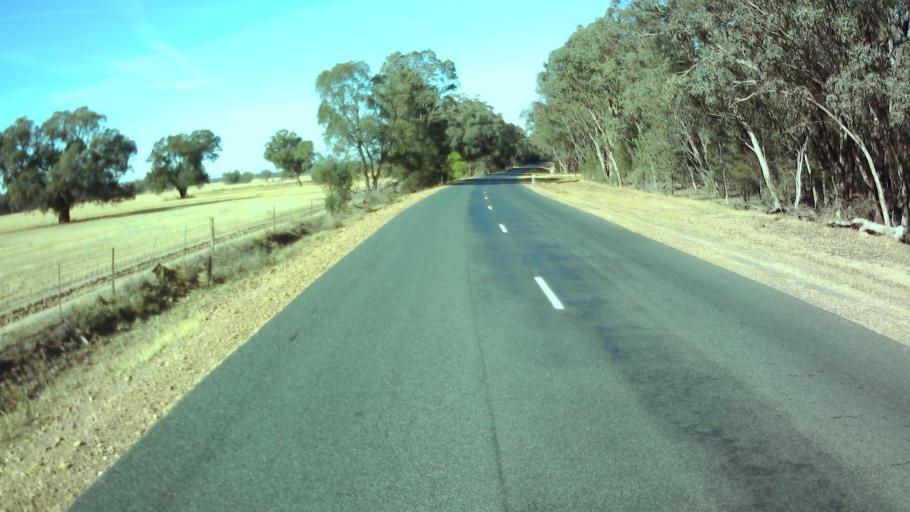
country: AU
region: New South Wales
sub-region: Weddin
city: Grenfell
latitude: -34.0101
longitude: 148.1194
